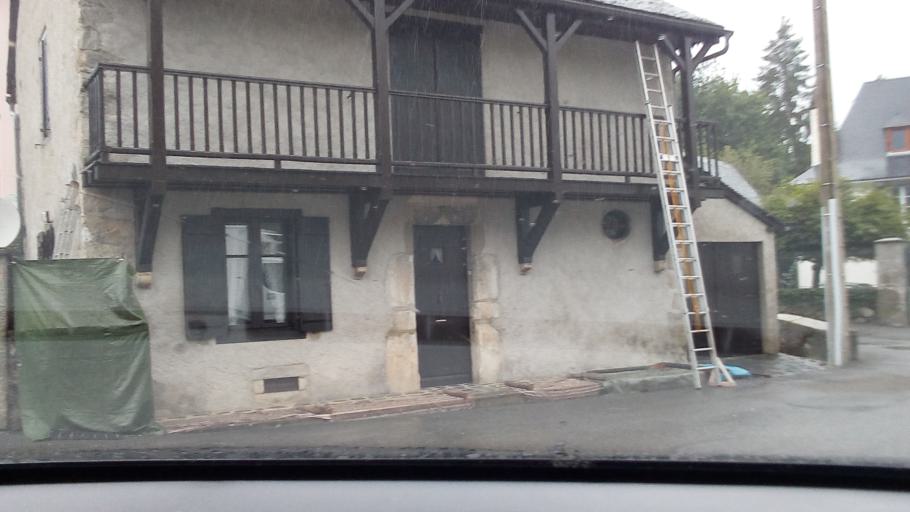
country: FR
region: Midi-Pyrenees
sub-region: Departement des Hautes-Pyrenees
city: Cauterets
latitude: 42.9553
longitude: -0.2125
